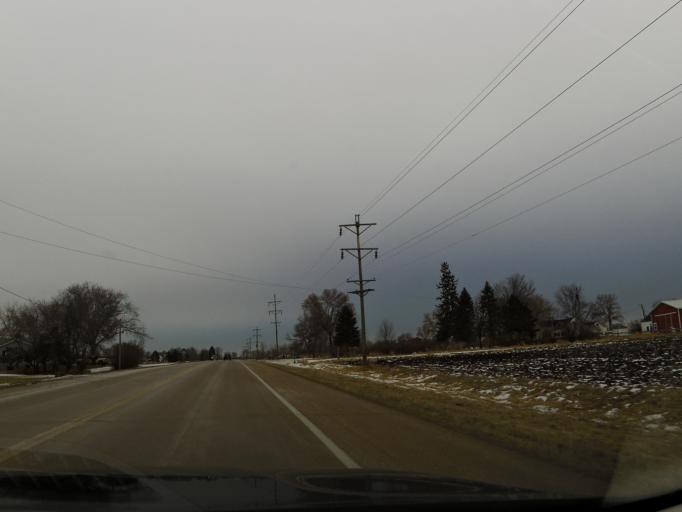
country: US
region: Minnesota
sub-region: Carver County
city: Watertown
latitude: 44.9280
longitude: -93.8316
